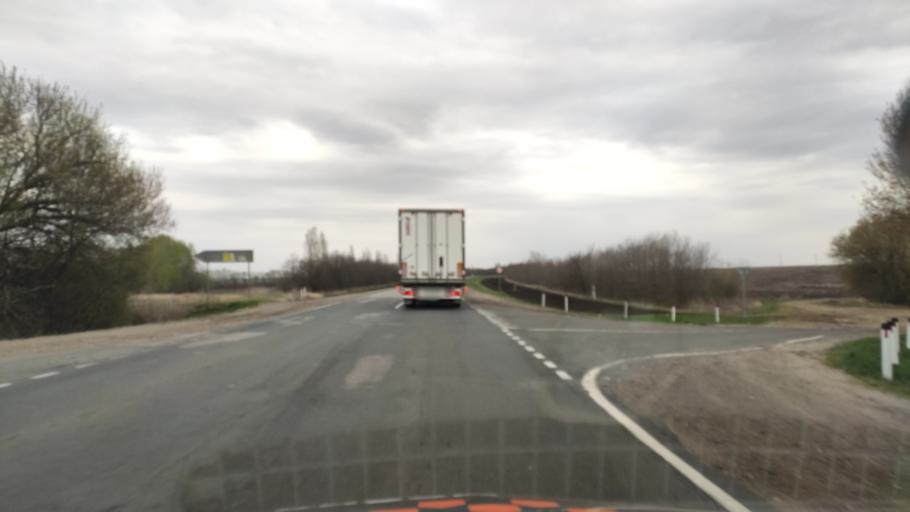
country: RU
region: Voronezj
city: Nizhnedevitsk
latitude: 51.5756
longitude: 38.3229
